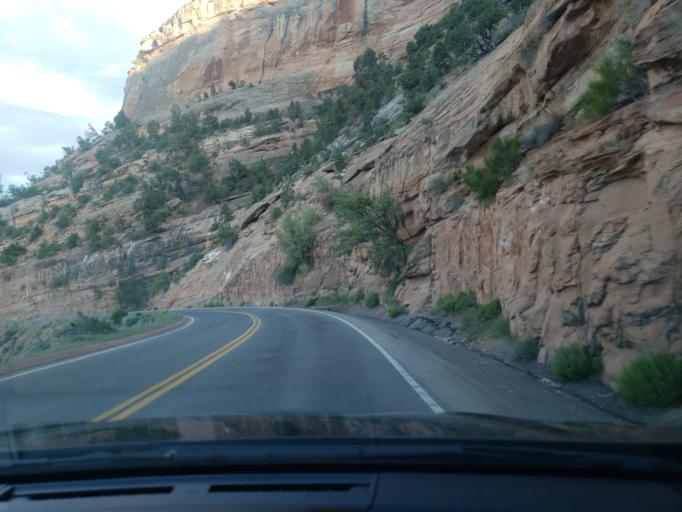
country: US
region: Colorado
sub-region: Mesa County
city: Fruita
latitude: 39.1153
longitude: -108.7274
